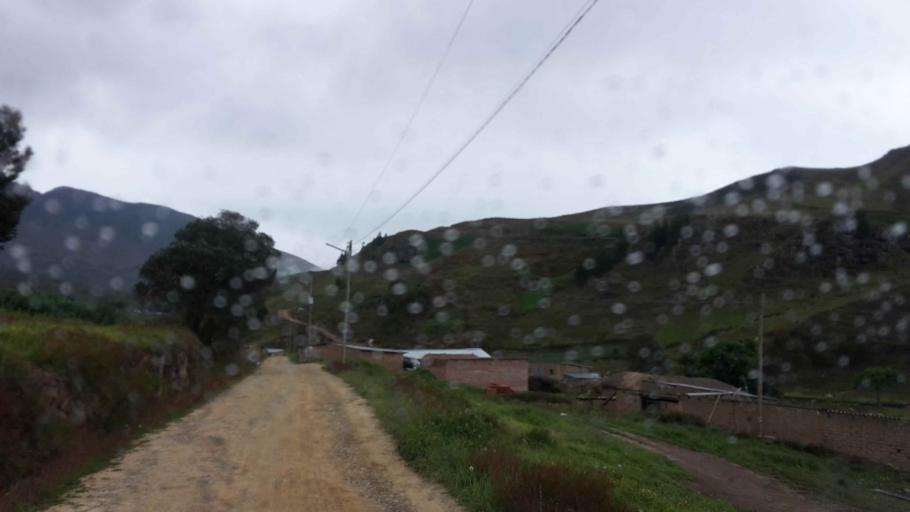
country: BO
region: Cochabamba
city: Cochabamba
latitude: -17.1352
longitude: -66.1046
